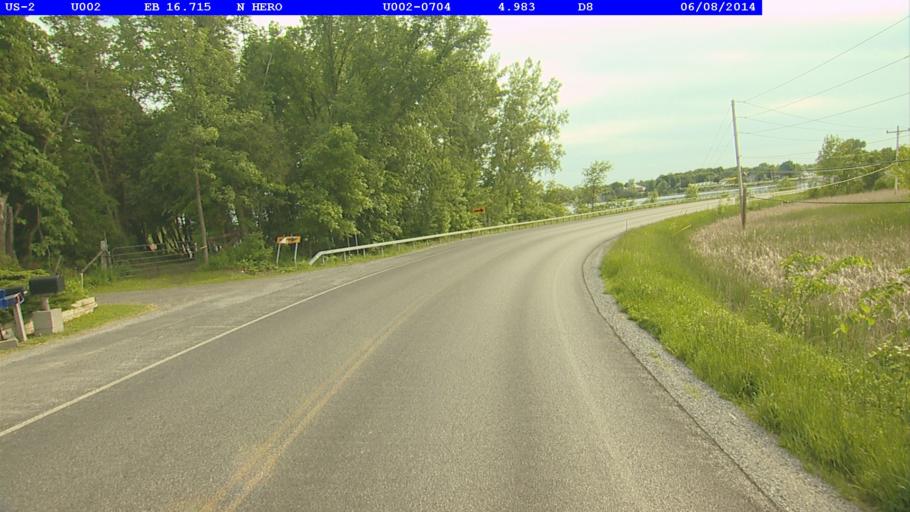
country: US
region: Vermont
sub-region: Grand Isle County
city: North Hero
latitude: 44.8225
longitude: -73.2801
